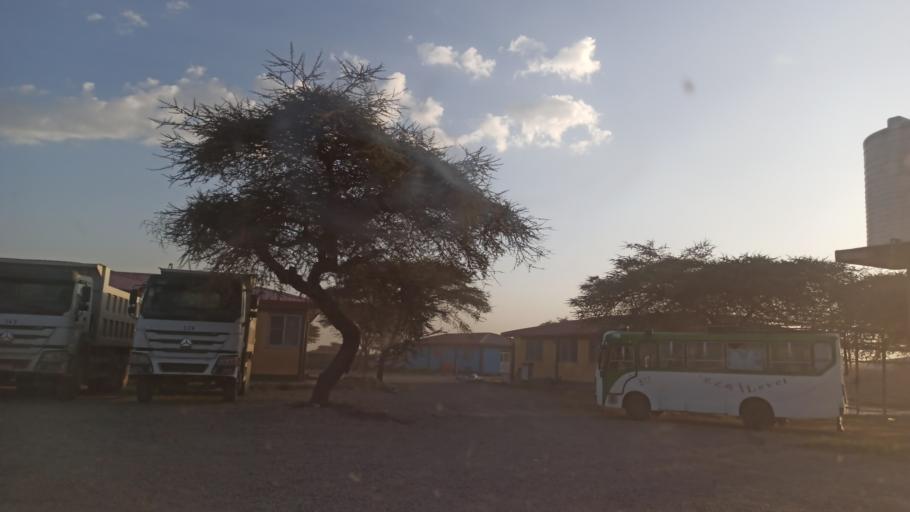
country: ET
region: Oromiya
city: Ziway
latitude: 7.7024
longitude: 38.6535
